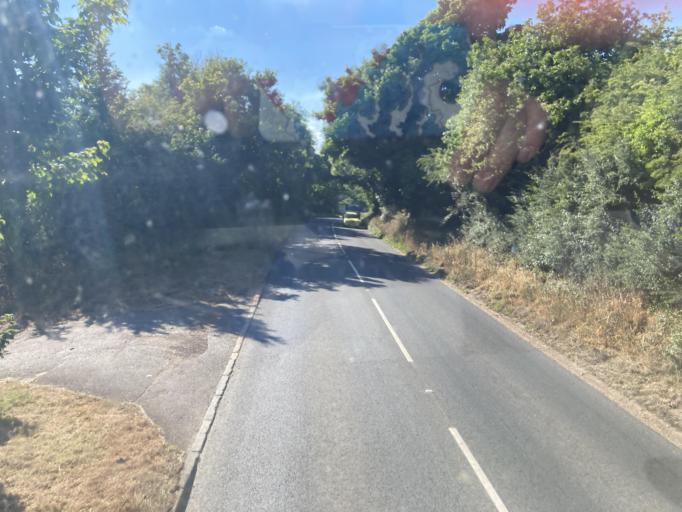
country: GB
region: England
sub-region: Isle of Wight
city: Newport
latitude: 50.6734
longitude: -1.2795
